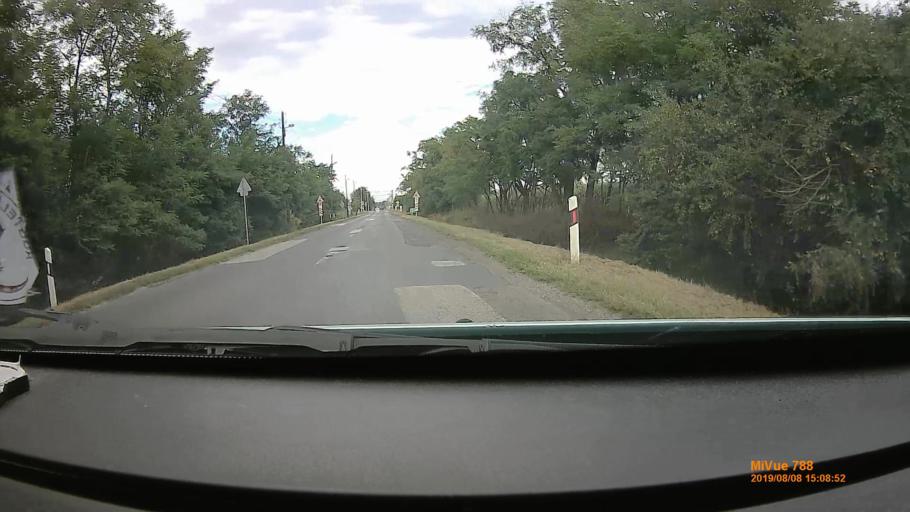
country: HU
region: Szabolcs-Szatmar-Bereg
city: Tunyogmatolcs
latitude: 47.9607
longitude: 22.4433
